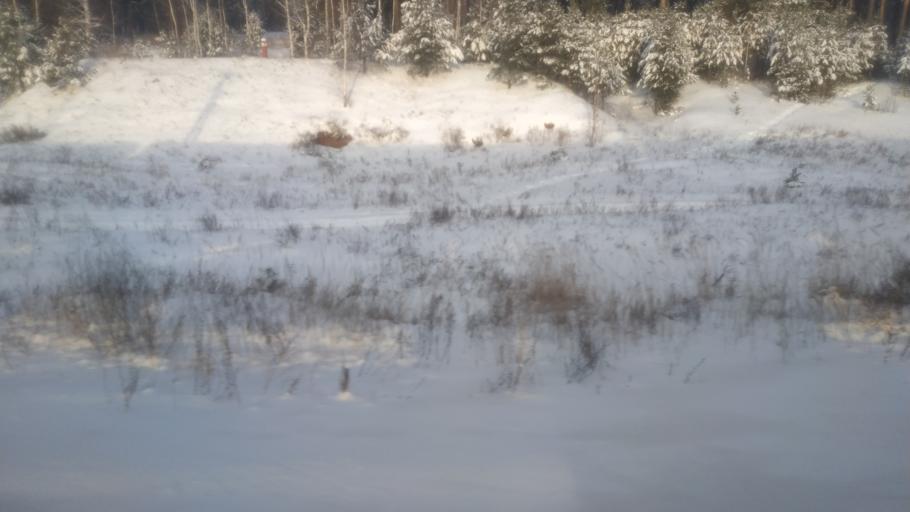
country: RU
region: Kirov
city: Krasnaya Polyana
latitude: 56.2464
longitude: 51.1656
